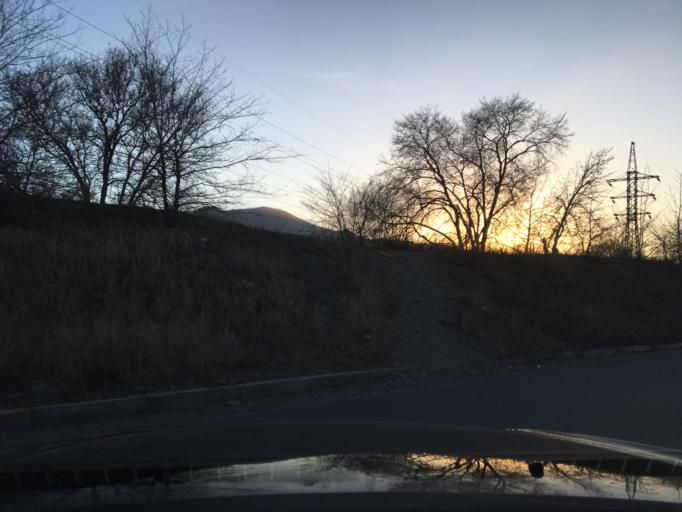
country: MN
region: Ulaanbaatar
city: Ulaanbaatar
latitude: 47.8927
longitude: 106.9156
